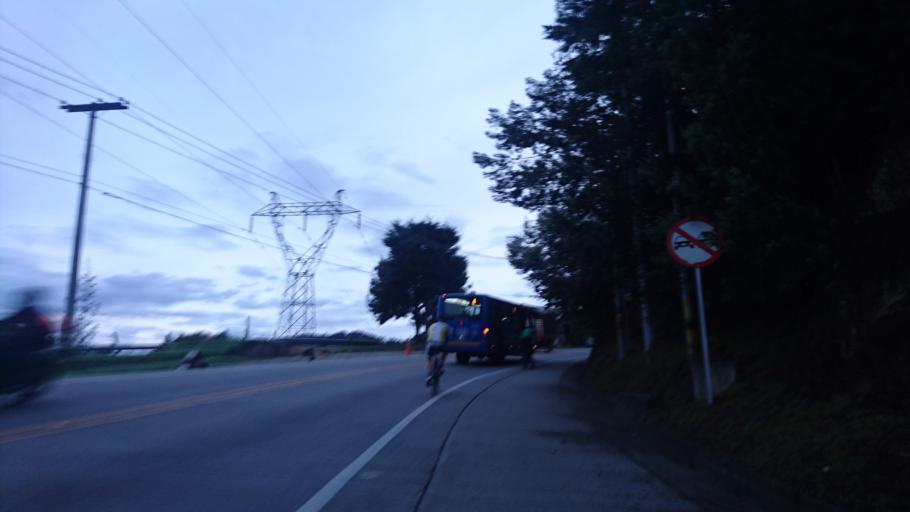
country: CO
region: Bogota D.C.
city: Barrio San Luis
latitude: 4.6757
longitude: -74.0272
